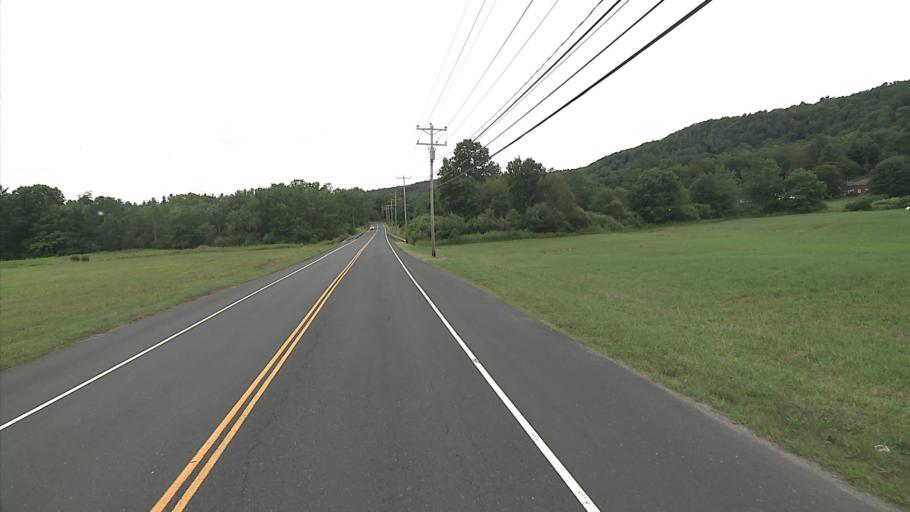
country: US
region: Connecticut
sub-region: Litchfield County
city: Winsted
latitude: 41.9768
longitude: -73.0460
